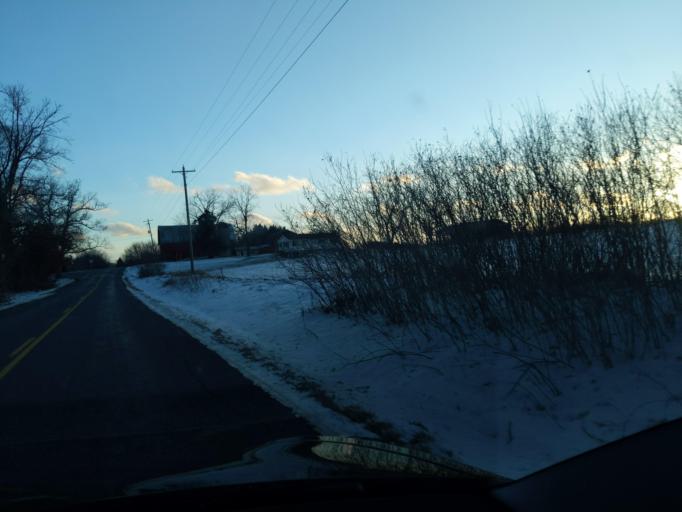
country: US
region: Michigan
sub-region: Ingham County
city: Stockbridge
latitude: 42.4553
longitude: -84.2246
